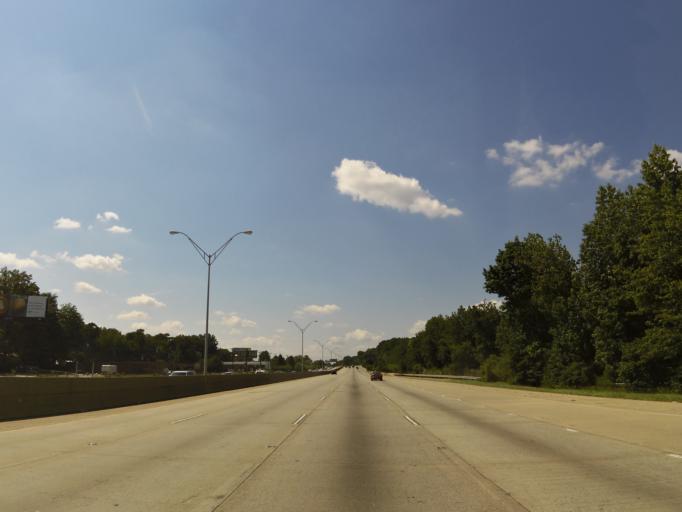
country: US
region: North Carolina
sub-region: Mecklenburg County
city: Charlotte
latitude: 35.2398
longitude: -80.9243
